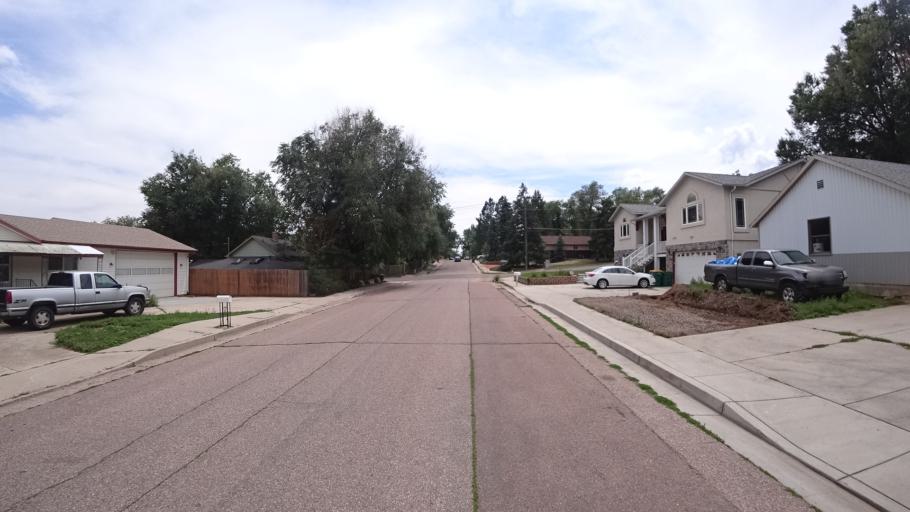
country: US
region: Colorado
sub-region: El Paso County
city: Colorado Springs
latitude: 38.8540
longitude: -104.8349
